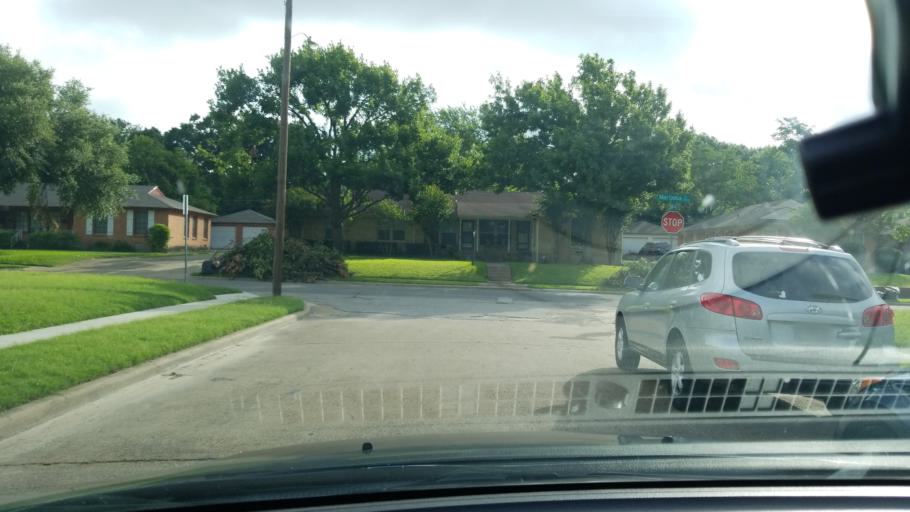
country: US
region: Texas
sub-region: Dallas County
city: Highland Park
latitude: 32.8250
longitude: -96.6919
